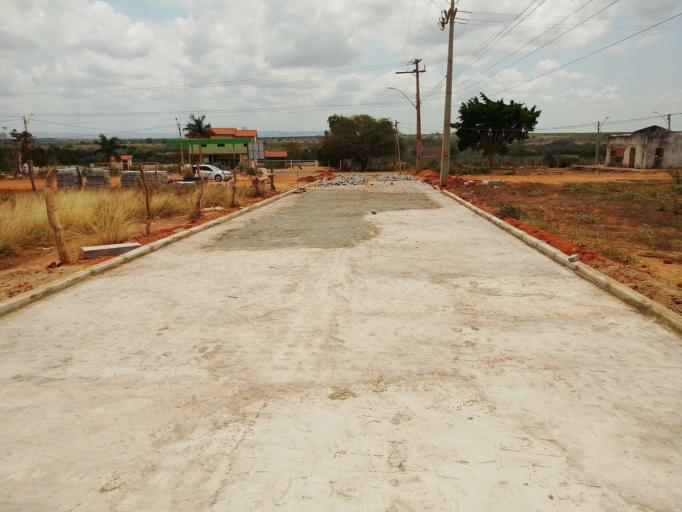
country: BR
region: Minas Gerais
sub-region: Sao Joao Do Paraiso
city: Sao Joao do Paraiso
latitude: -15.0297
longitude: -41.9323
